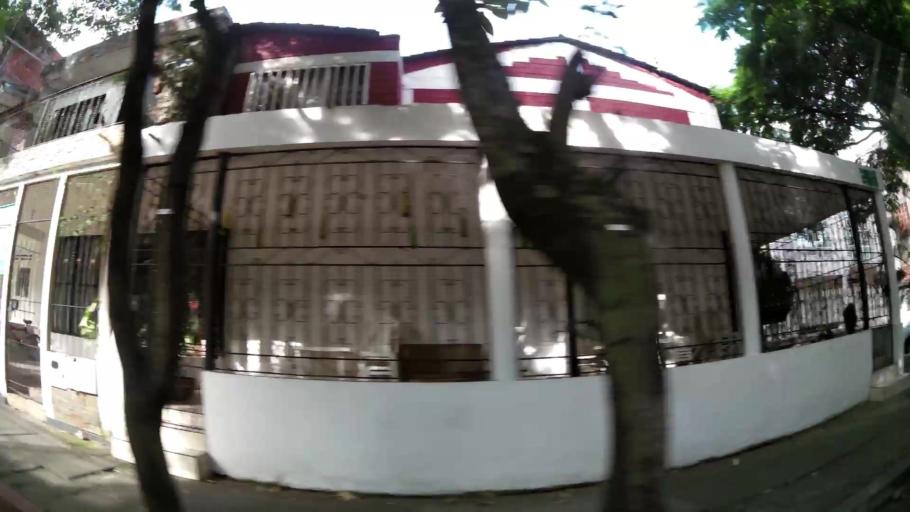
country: CO
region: Valle del Cauca
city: Cali
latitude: 3.4734
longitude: -76.4951
